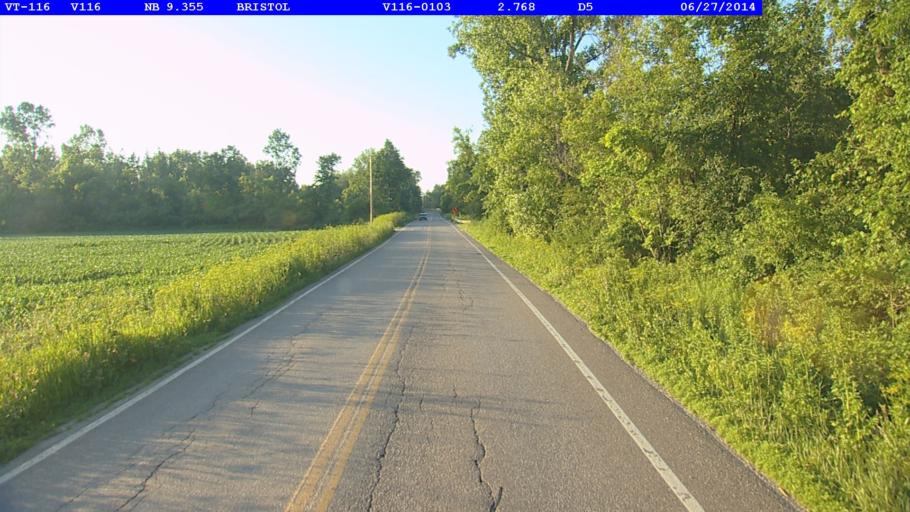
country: US
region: Vermont
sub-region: Addison County
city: Bristol
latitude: 44.0929
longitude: -73.0909
